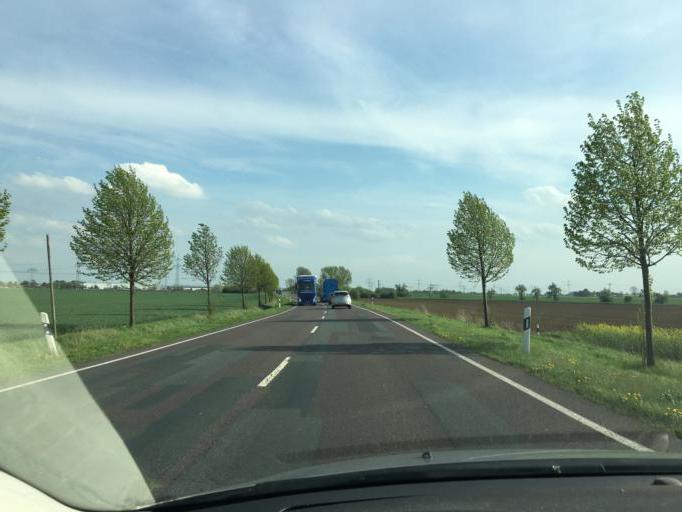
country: DE
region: Saxony-Anhalt
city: Meitzendorf
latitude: 52.2190
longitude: 11.5403
